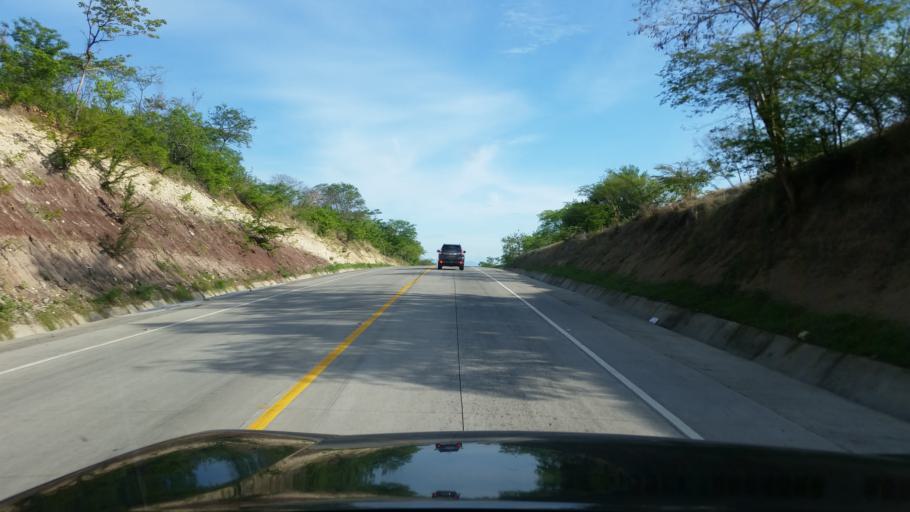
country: NI
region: Leon
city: Nagarote
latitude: 12.1719
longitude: -86.6649
